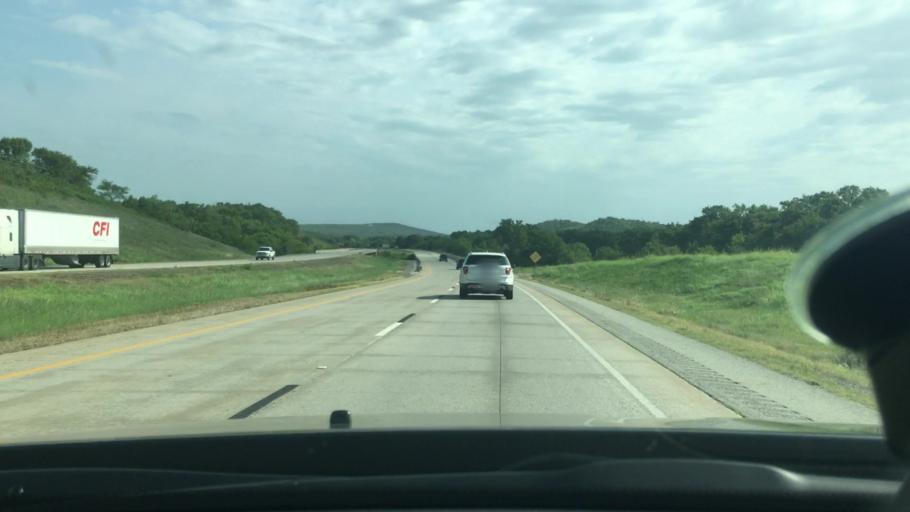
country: US
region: Oklahoma
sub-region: Atoka County
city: Atoka
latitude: 34.4379
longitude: -96.0748
